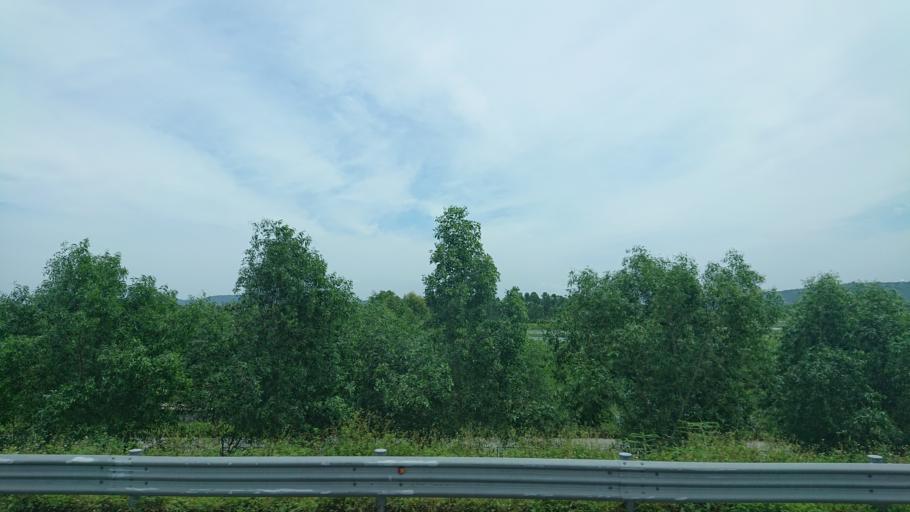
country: VN
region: Hai Phong
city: Tien Lang
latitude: 20.7714
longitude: 106.5870
